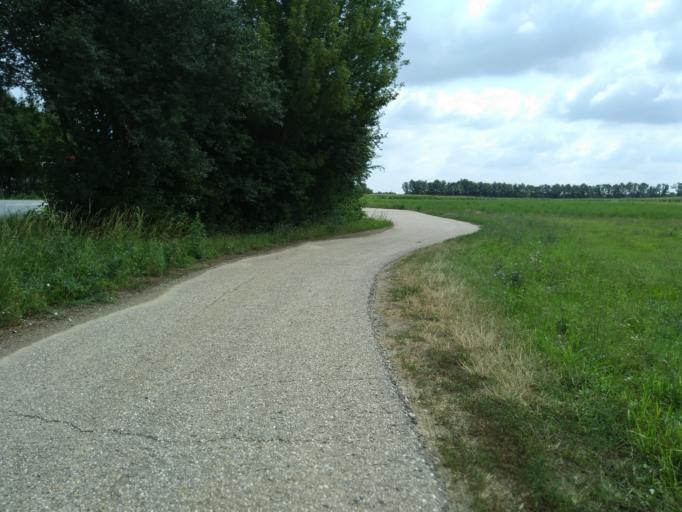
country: AT
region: Lower Austria
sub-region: Politischer Bezirk Ganserndorf
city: Gross-Schweinbarth
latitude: 48.4026
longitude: 16.6443
